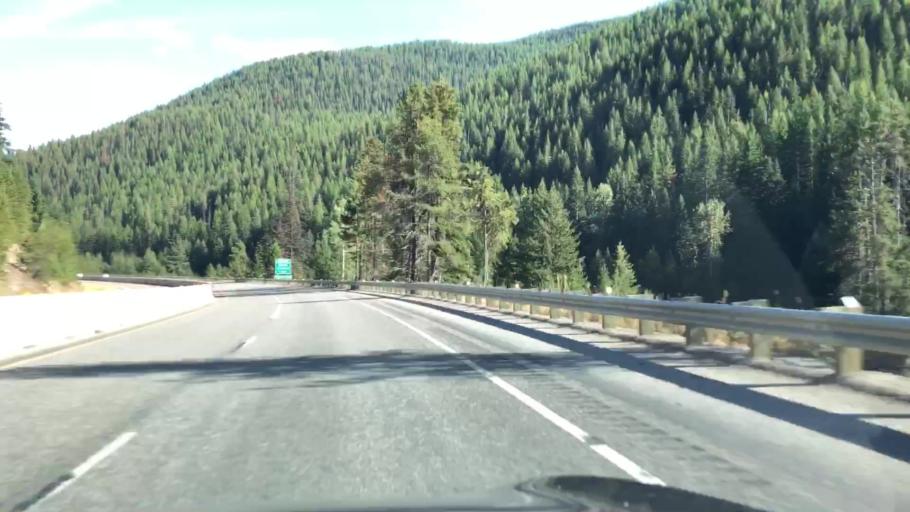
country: US
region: Montana
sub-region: Sanders County
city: Thompson Falls
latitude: 47.3956
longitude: -115.4546
